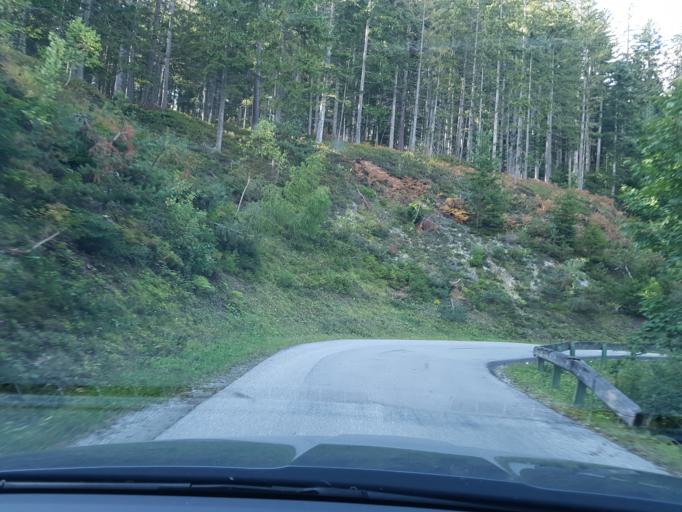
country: AT
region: Salzburg
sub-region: Politischer Bezirk Sankt Johann im Pongau
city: Radstadt
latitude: 47.3958
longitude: 13.4891
